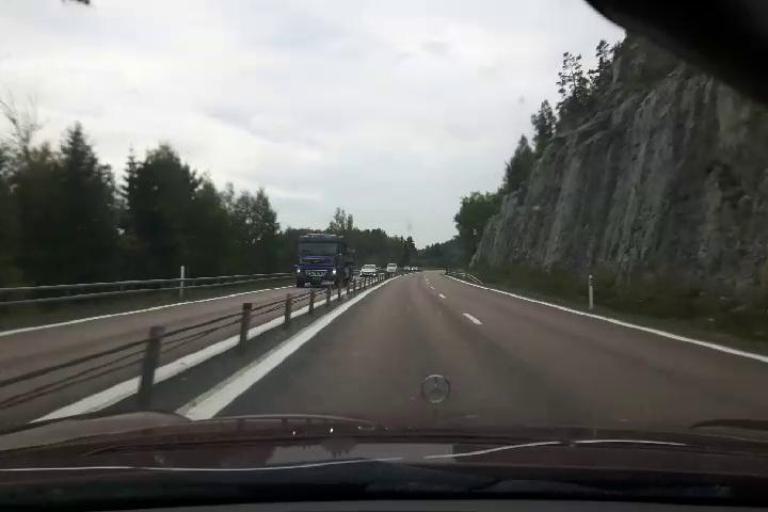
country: SE
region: Vaesternorrland
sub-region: Haernoesands Kommun
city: Haernoesand
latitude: 62.8194
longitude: 17.9696
